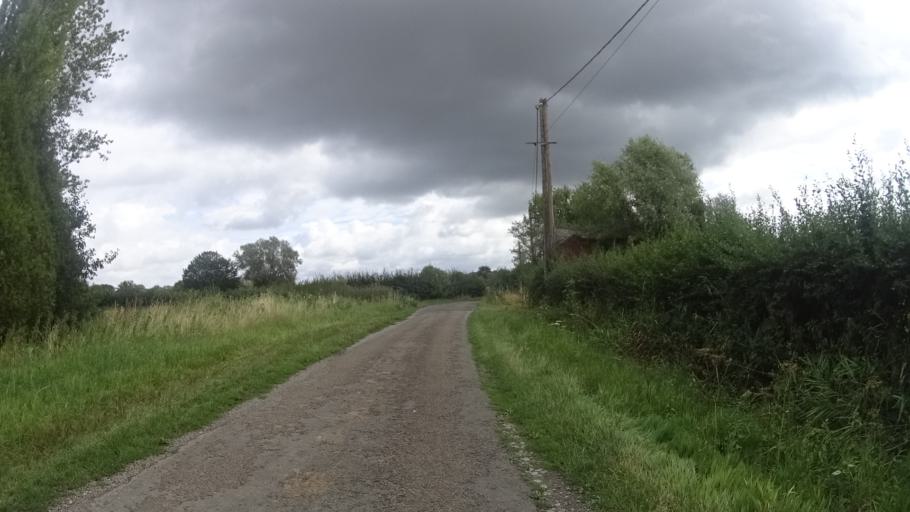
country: FR
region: Nord-Pas-de-Calais
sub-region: Departement du Nord
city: Landrecies
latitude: 50.1295
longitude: 3.7212
